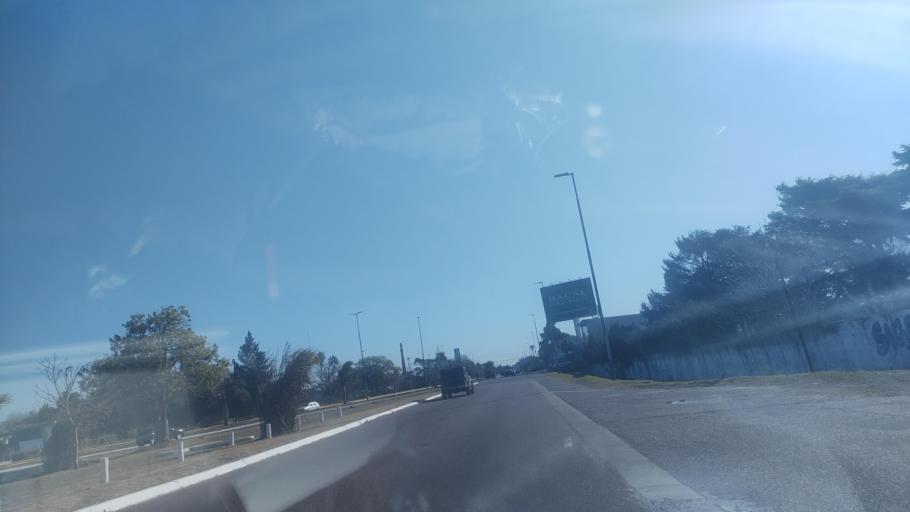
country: AR
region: Buenos Aires
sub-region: Partido de La Plata
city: La Plata
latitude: -34.8931
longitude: -57.9925
